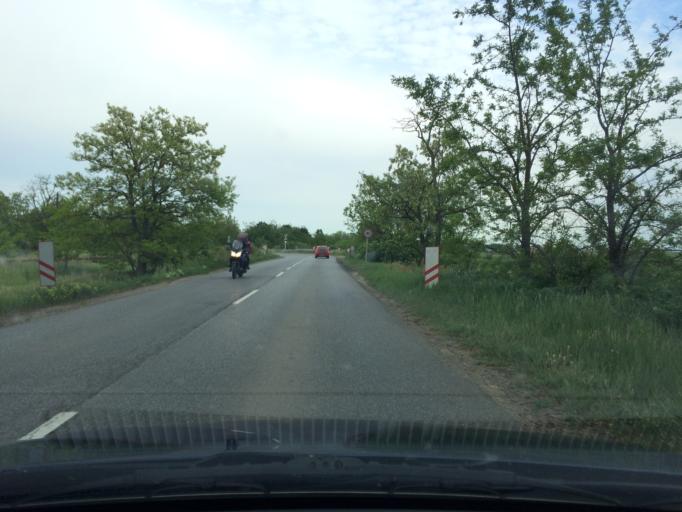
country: HU
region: Szabolcs-Szatmar-Bereg
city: Tiszavasvari
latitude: 47.9211
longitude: 21.3923
